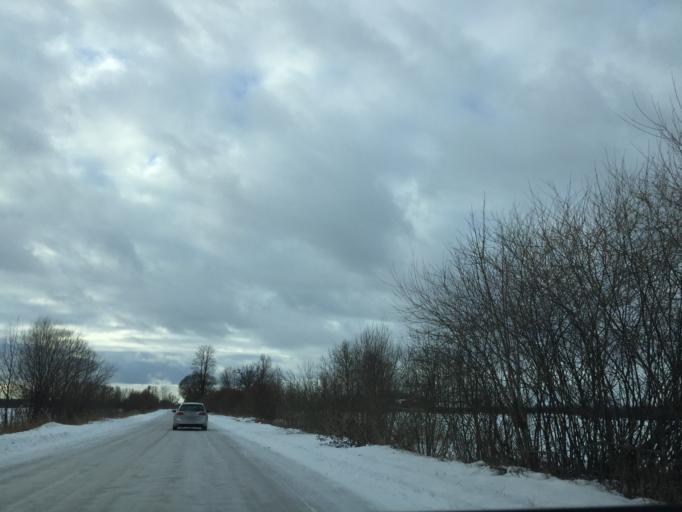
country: LV
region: Lielvarde
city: Lielvarde
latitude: 56.6158
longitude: 24.7696
